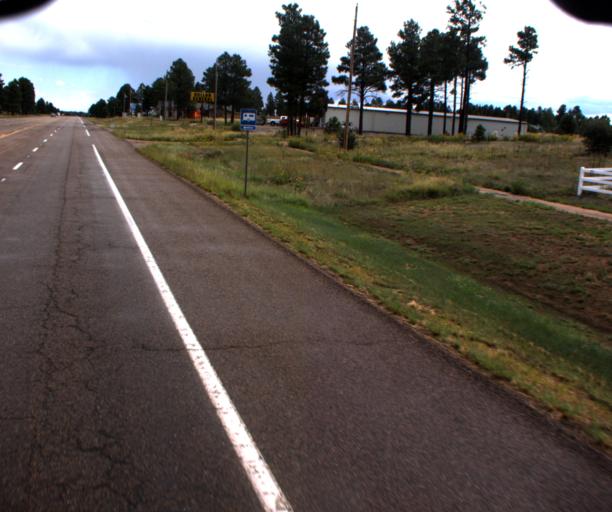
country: US
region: Arizona
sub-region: Navajo County
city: Heber-Overgaard
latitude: 34.3899
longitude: -110.5390
